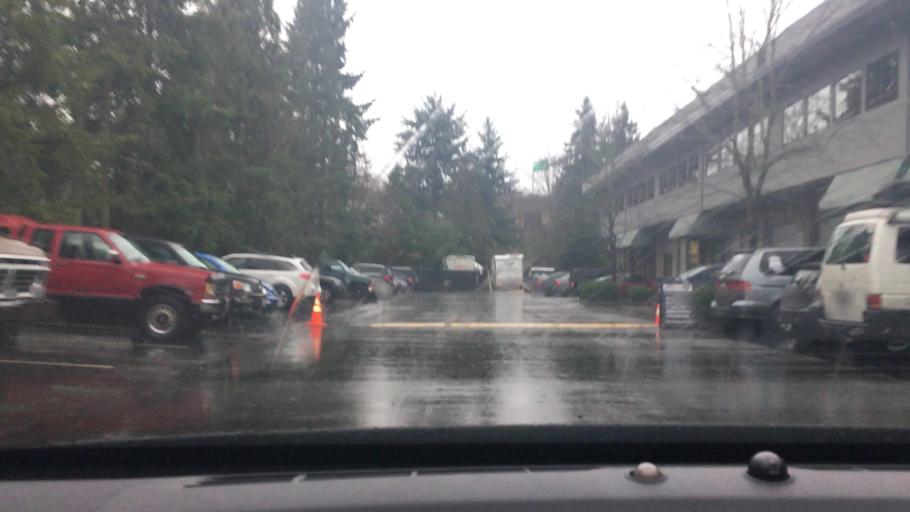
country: US
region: Washington
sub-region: King County
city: Redmond
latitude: 47.6291
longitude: -122.1495
